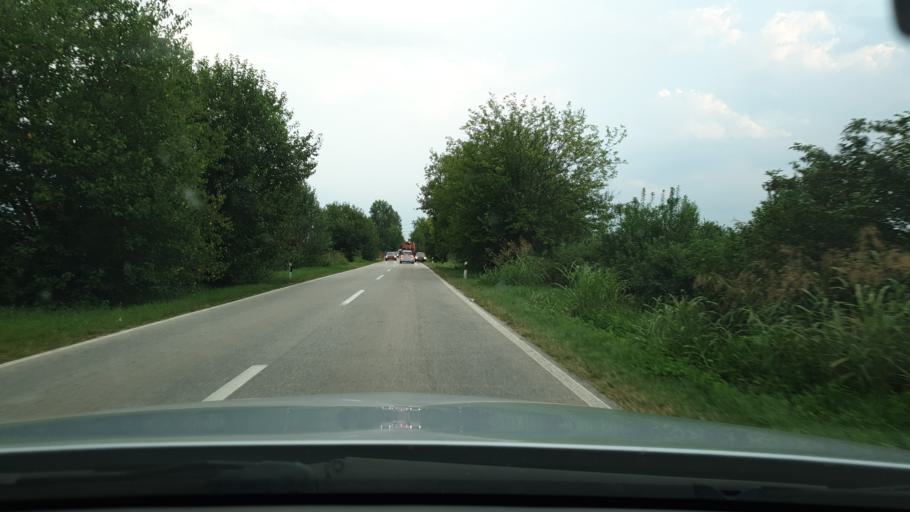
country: RS
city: Pavlis
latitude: 45.0339
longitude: 21.2803
